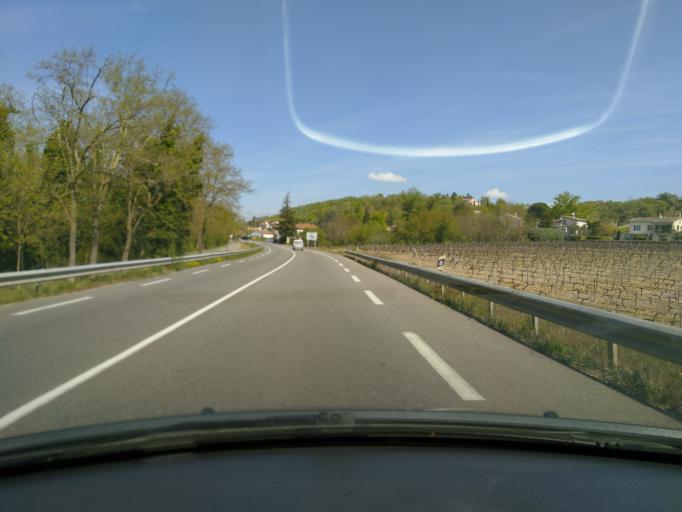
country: FR
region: Rhone-Alpes
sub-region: Departement de l'Ardeche
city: Ruoms
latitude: 44.4473
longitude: 4.3489
